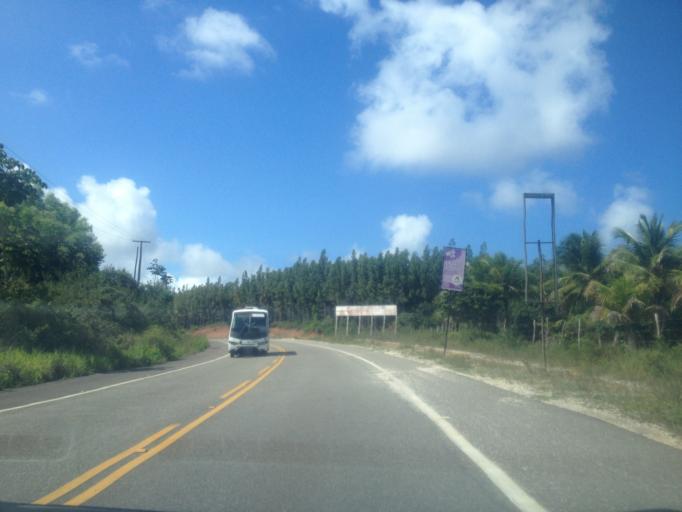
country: BR
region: Sergipe
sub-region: Indiaroba
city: Indiaroba
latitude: -11.4860
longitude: -37.4716
